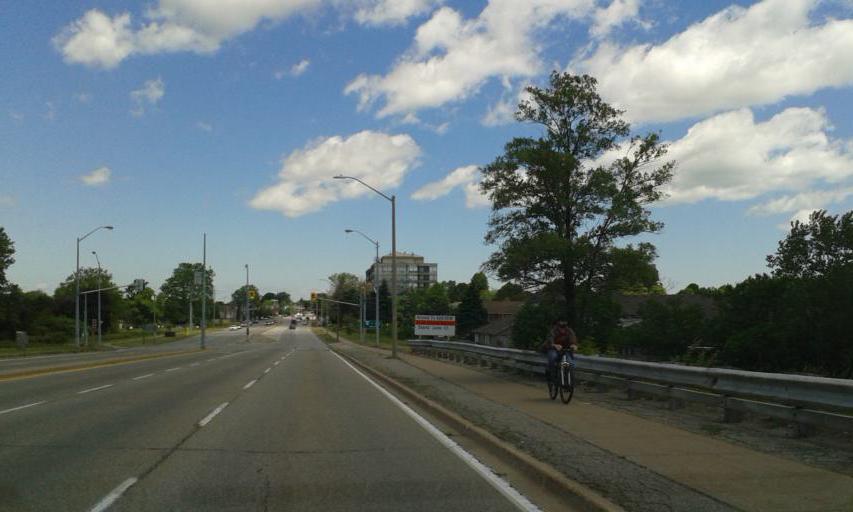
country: CA
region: Ontario
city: Niagara Falls
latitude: 43.0965
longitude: -79.1108
